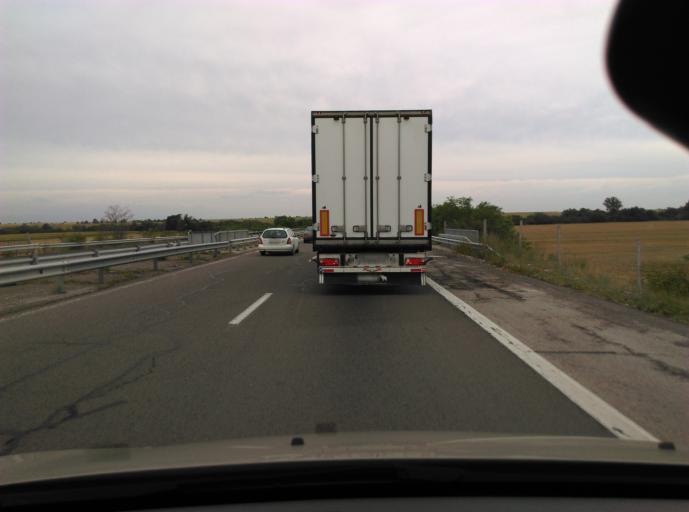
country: BG
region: Stara Zagora
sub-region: Obshtina Chirpan
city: Chirpan
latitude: 42.1926
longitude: 25.2157
